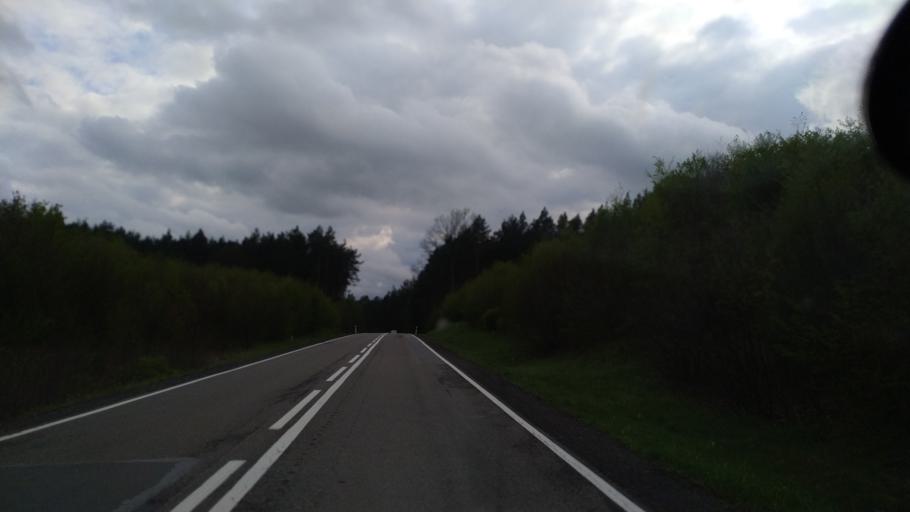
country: PL
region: Pomeranian Voivodeship
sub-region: Powiat kwidzynski
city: Ryjewo
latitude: 53.8234
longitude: 18.9846
